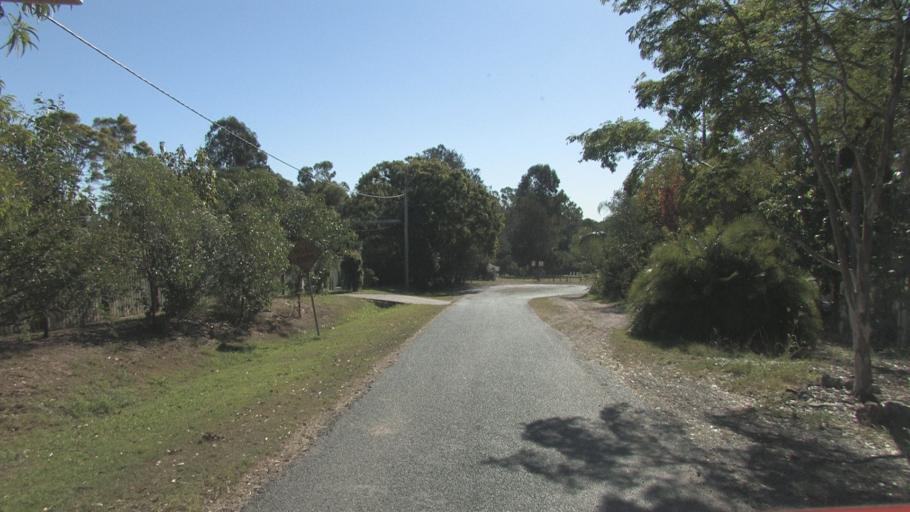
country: AU
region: Queensland
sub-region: Logan
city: Logan Reserve
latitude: -27.7426
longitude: 153.1225
